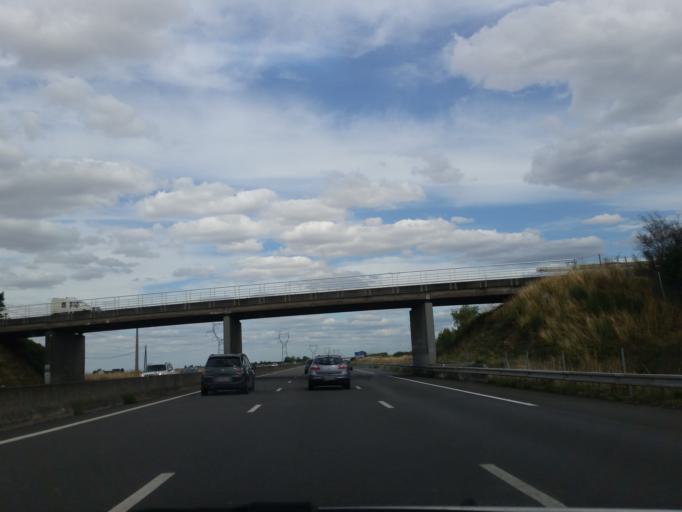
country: FR
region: Centre
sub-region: Departement du Loir-et-Cher
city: Herbault
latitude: 47.6131
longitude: 1.1474
